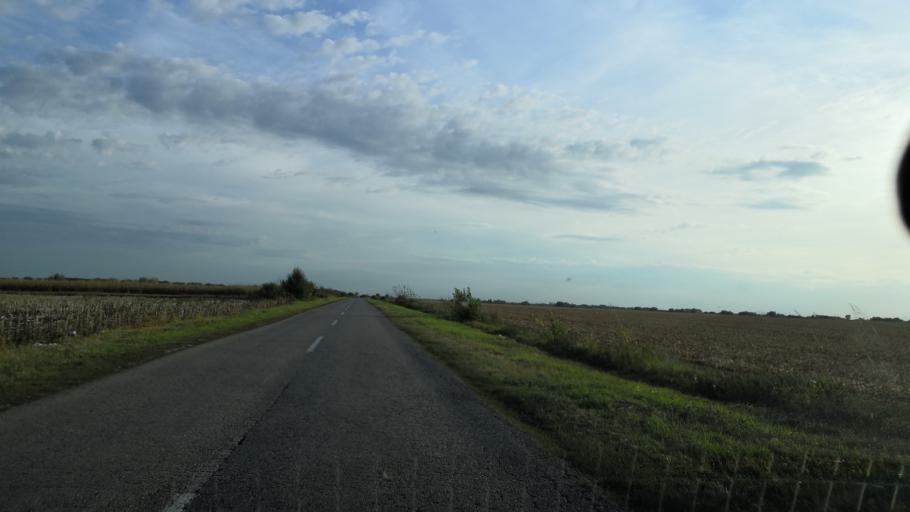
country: RS
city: Novi Karlovci
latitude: 45.0432
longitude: 20.1753
